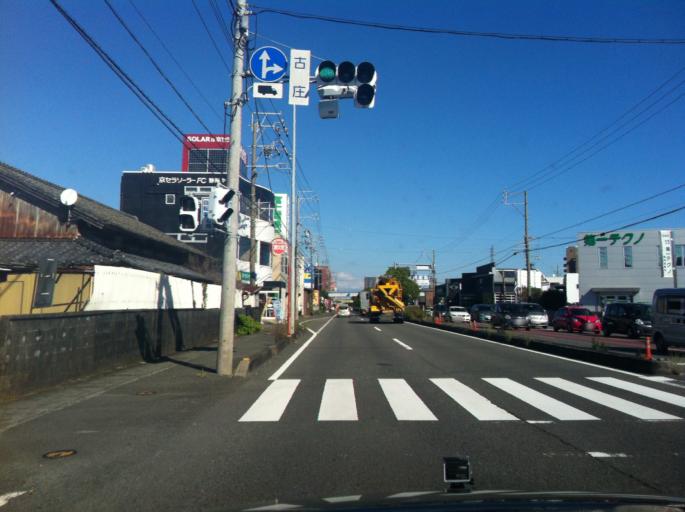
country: JP
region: Shizuoka
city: Shizuoka-shi
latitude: 34.9915
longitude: 138.4192
